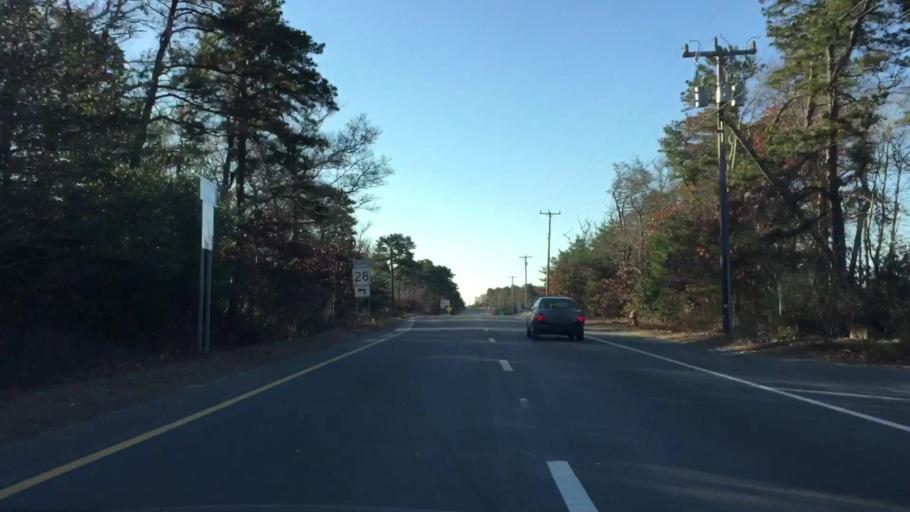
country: US
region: Massachusetts
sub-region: Barnstable County
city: Bourne
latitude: 41.7312
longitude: -70.5844
